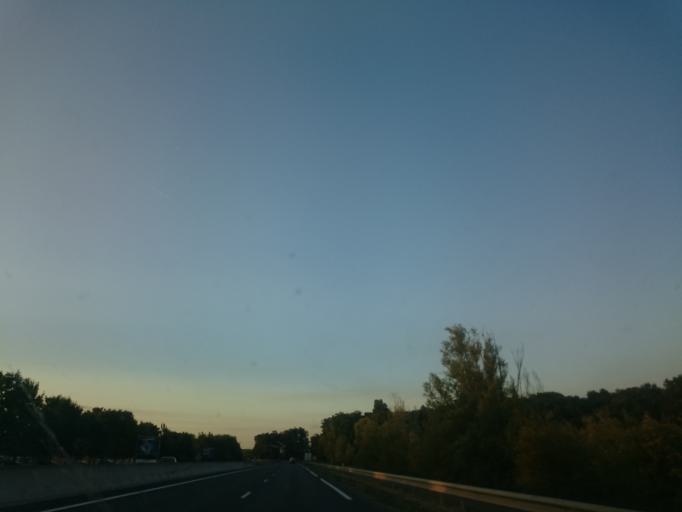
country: FR
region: Ile-de-France
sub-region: Departement de l'Essonne
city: Marolles-en-Hurepoix
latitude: 48.5842
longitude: 2.3058
